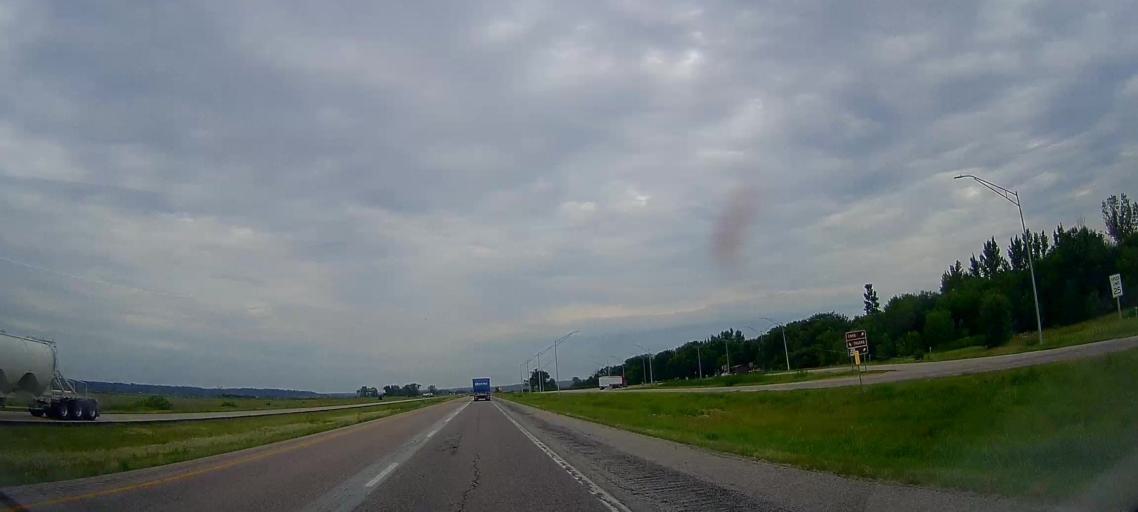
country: US
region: Iowa
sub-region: Harrison County
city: Missouri Valley
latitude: 41.5934
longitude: -95.9543
